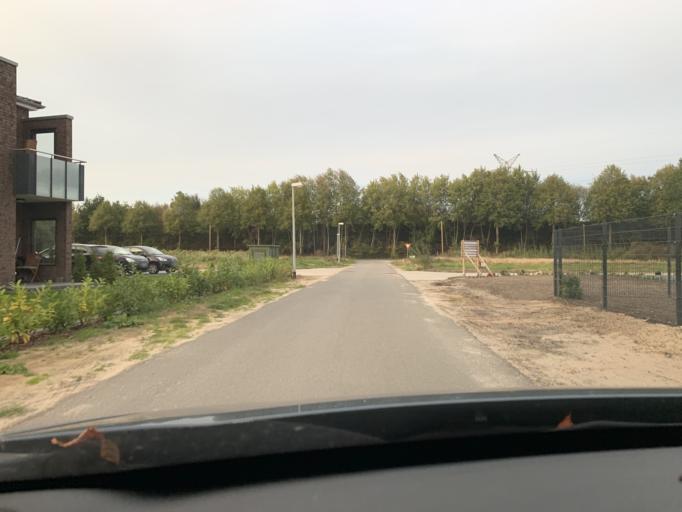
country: DE
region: Lower Saxony
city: Westerstede
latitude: 53.2537
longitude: 7.9512
